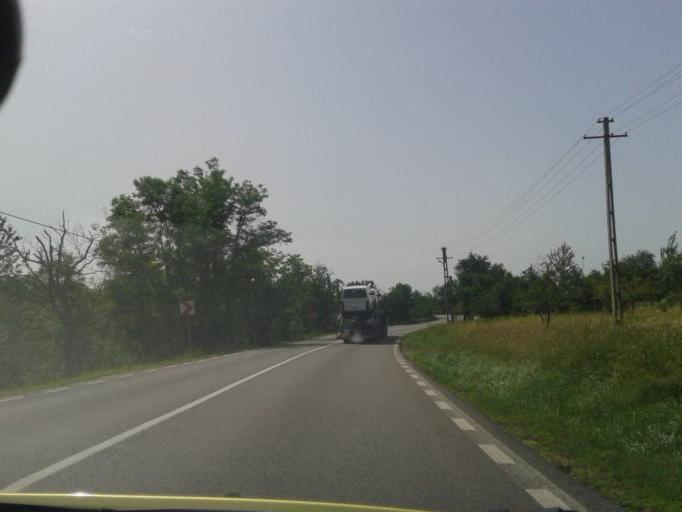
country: RO
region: Arges
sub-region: Comuna Cotmeana
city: Cotmeana
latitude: 44.9866
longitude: 24.6472
